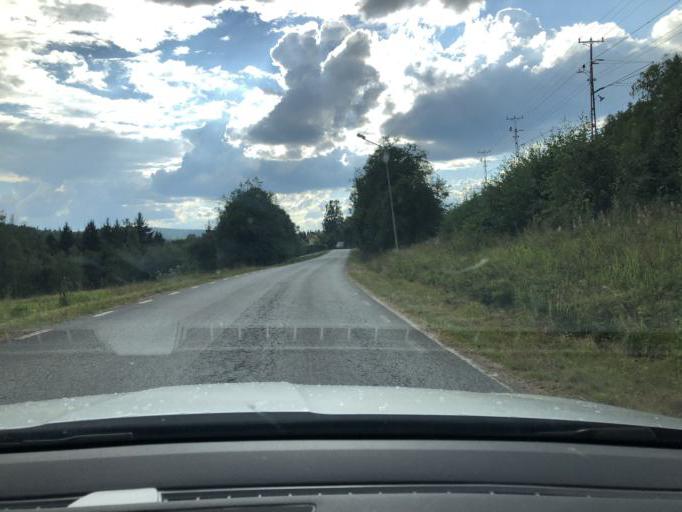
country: SE
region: Vaesternorrland
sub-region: Solleftea Kommun
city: Solleftea
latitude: 63.2125
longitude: 17.1923
